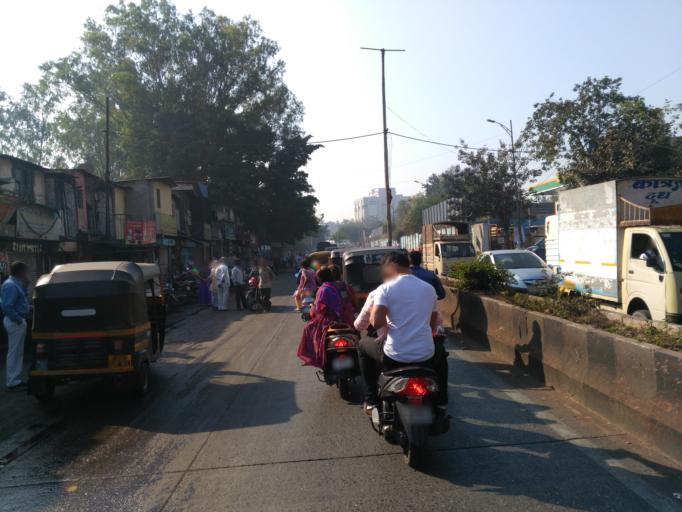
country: IN
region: Maharashtra
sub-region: Pune Division
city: Pune
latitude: 18.4963
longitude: 73.8693
